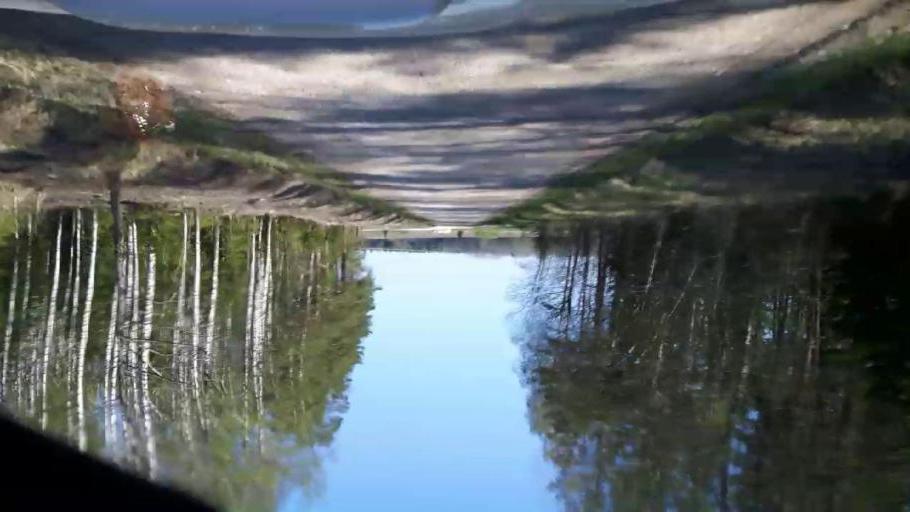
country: EE
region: Paernumaa
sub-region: Sindi linn
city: Sindi
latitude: 58.4746
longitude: 24.7498
